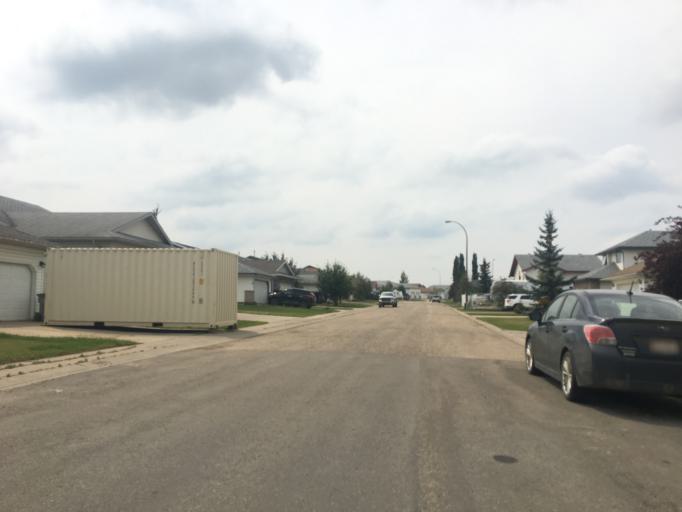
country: CA
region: Alberta
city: Grande Prairie
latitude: 55.1524
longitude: -118.8134
